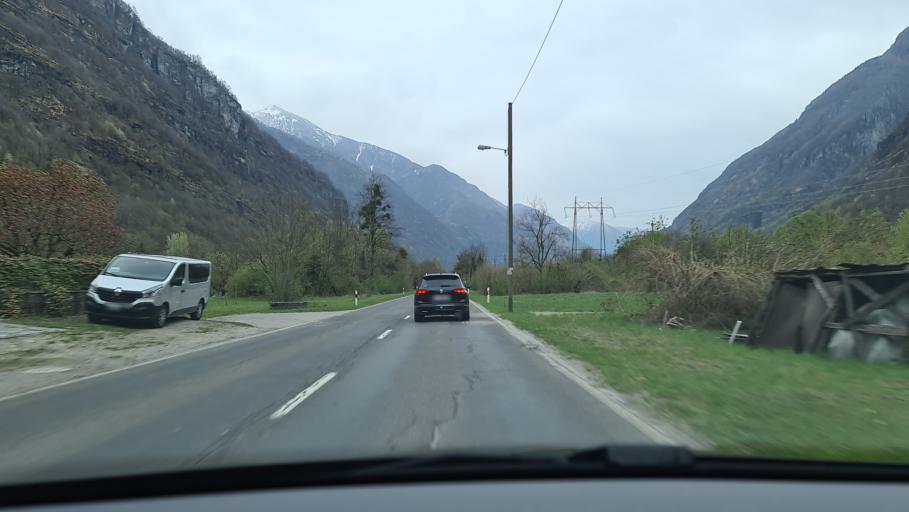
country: CH
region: Ticino
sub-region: Vallemaggia District
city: Cevio
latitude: 46.2961
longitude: 8.6320
